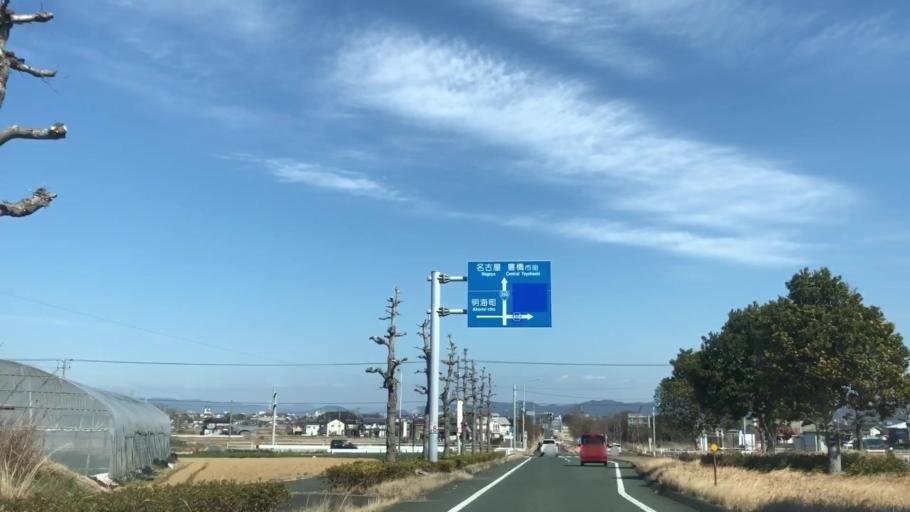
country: JP
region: Aichi
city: Toyohashi
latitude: 34.7120
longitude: 137.3592
